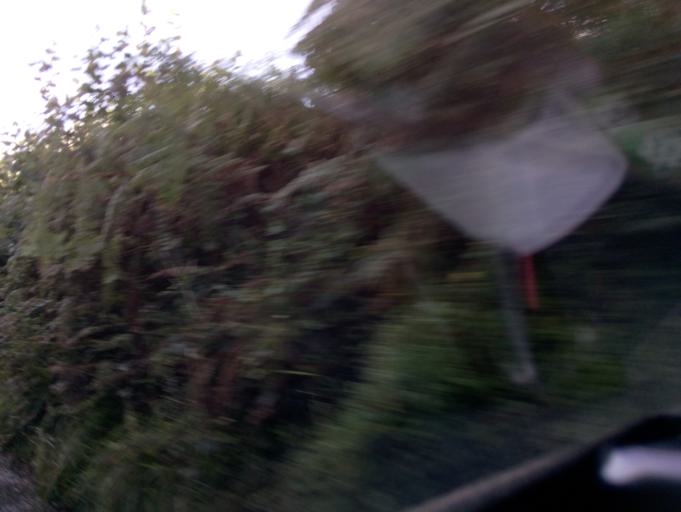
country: GB
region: England
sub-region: Devon
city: Dartmouth
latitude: 50.3407
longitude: -3.6069
